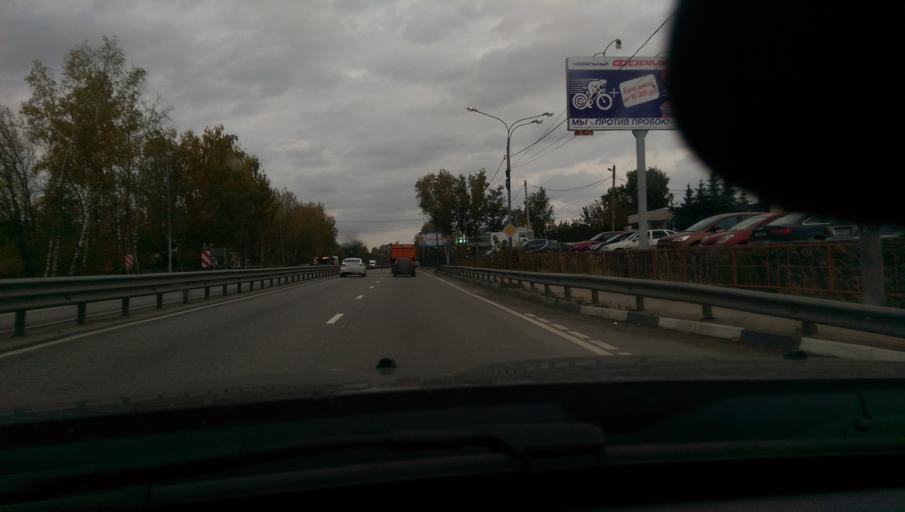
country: RU
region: Moscow
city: Vatutino
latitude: 55.9220
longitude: 37.6638
